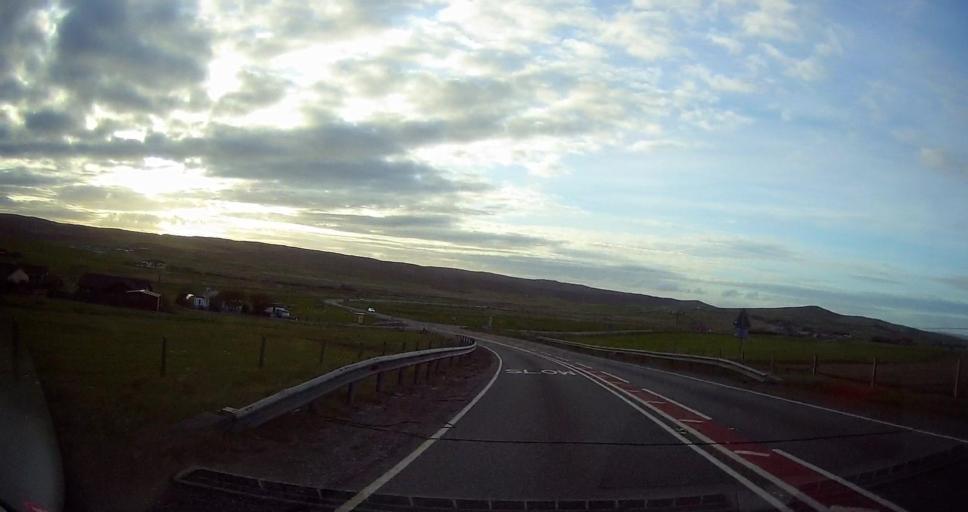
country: GB
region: Scotland
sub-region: Shetland Islands
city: Lerwick
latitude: 60.1850
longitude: -1.2248
